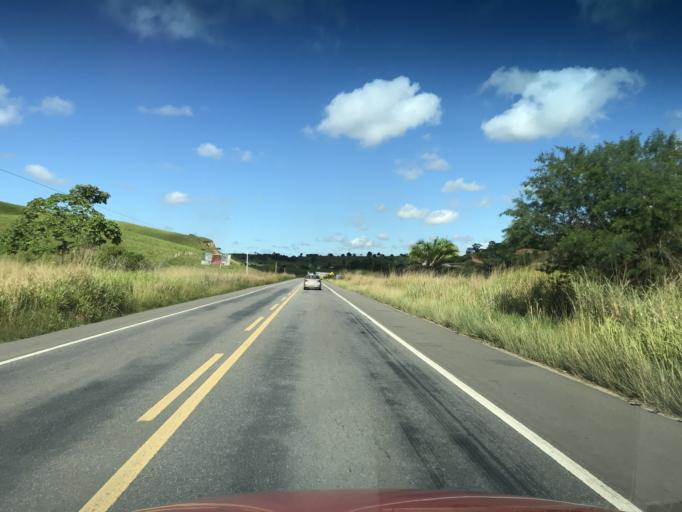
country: BR
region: Bahia
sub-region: Conceicao Do Almeida
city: Muritiba
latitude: -12.9287
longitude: -39.2526
